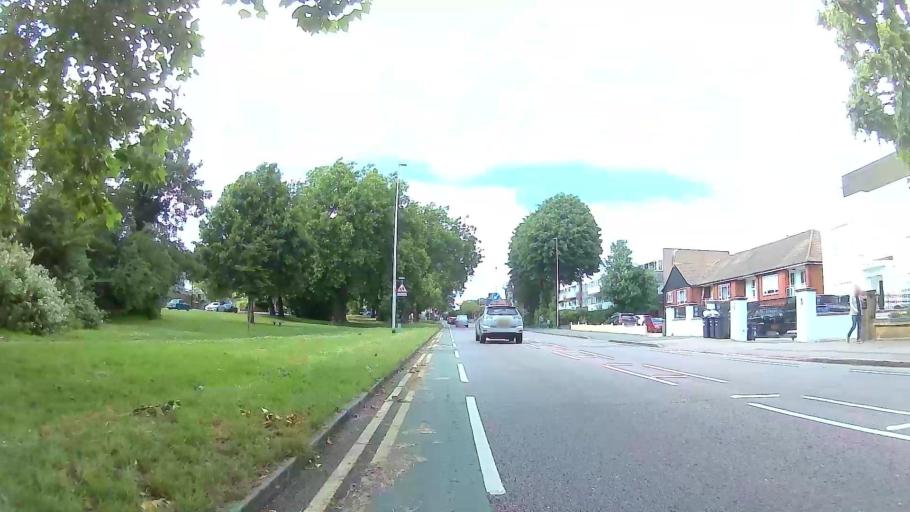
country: GB
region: England
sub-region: Greater London
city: Woodford Green
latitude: 51.5904
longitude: 0.0223
